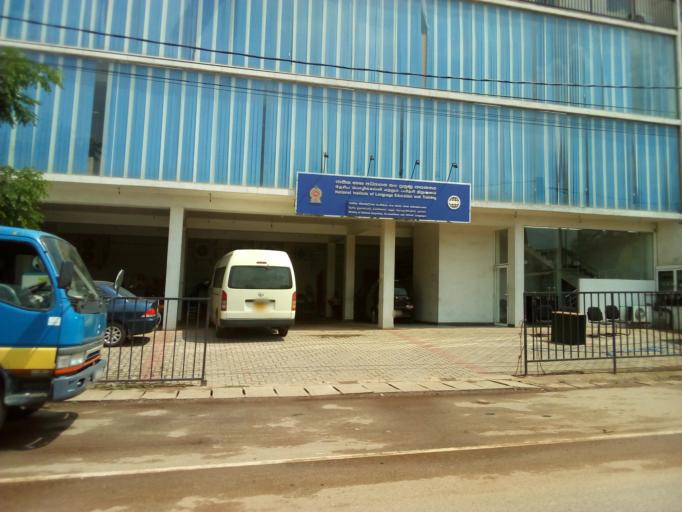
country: LK
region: Western
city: Homagama
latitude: 6.8389
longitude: 79.9777
